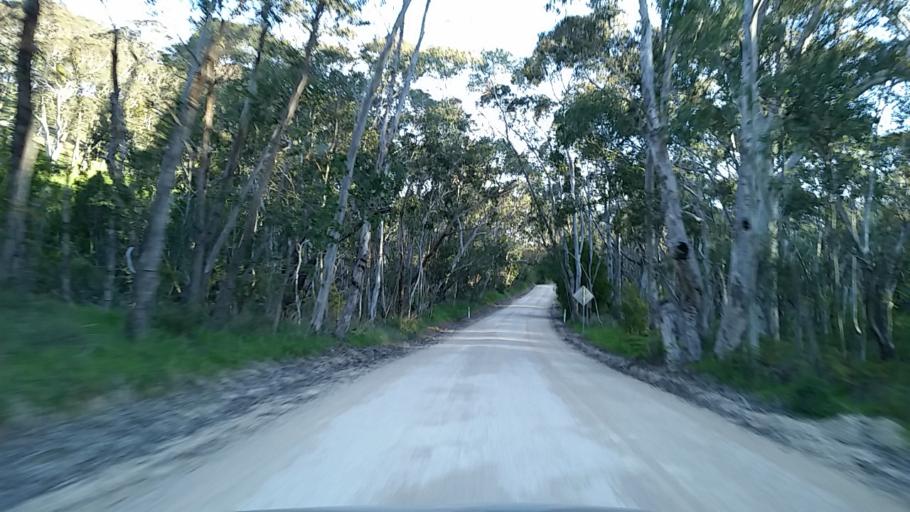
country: AU
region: South Australia
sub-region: Alexandrina
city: Mount Compass
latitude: -35.2741
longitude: 138.7014
